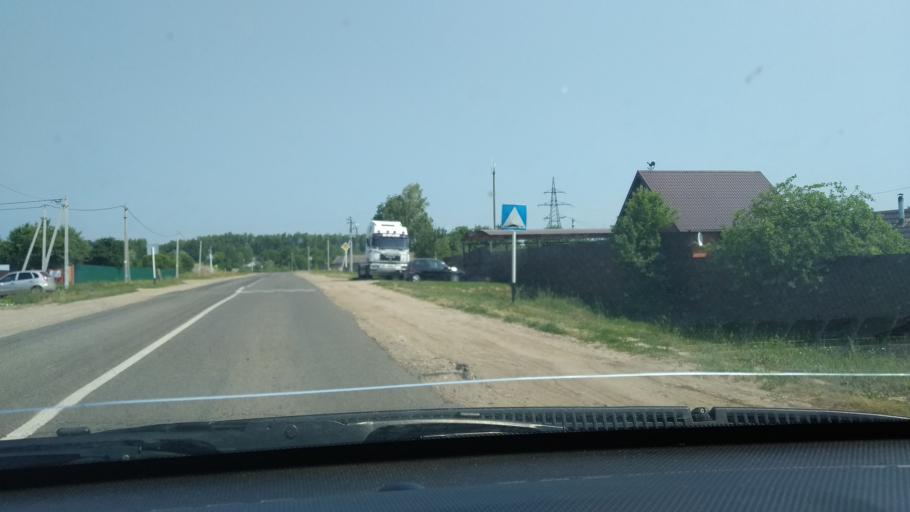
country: RU
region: Tatarstan
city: Osinovo
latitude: 55.9844
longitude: 48.8130
